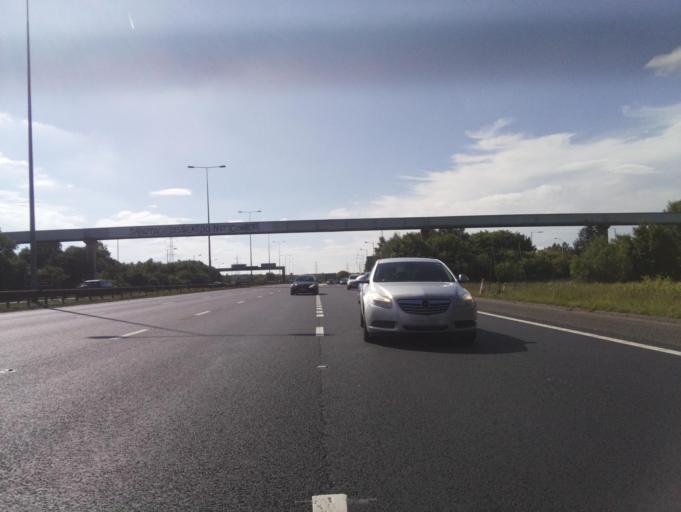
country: GB
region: England
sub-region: Borough of Bolton
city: Kearsley
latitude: 53.5305
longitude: -2.3742
